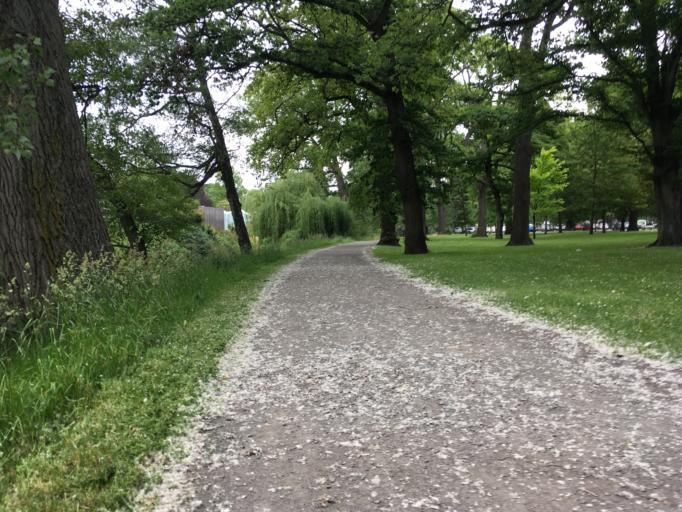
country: NZ
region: Canterbury
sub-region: Christchurch City
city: Christchurch
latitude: -43.5295
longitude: 172.6239
